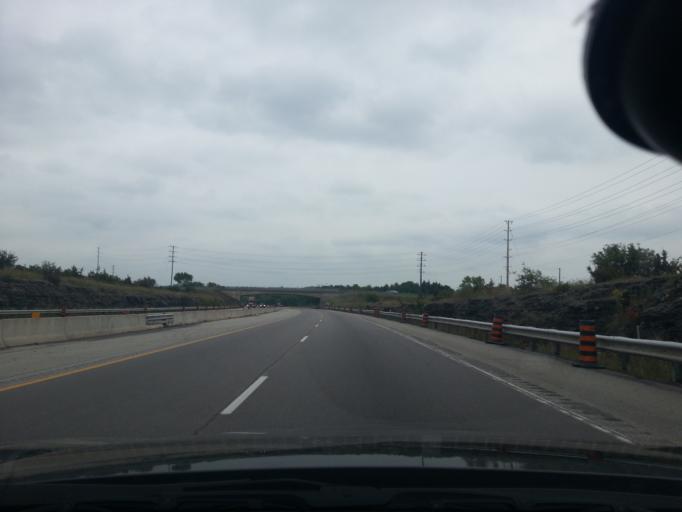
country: CA
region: Ontario
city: Skatepark
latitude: 44.2656
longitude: -76.9481
